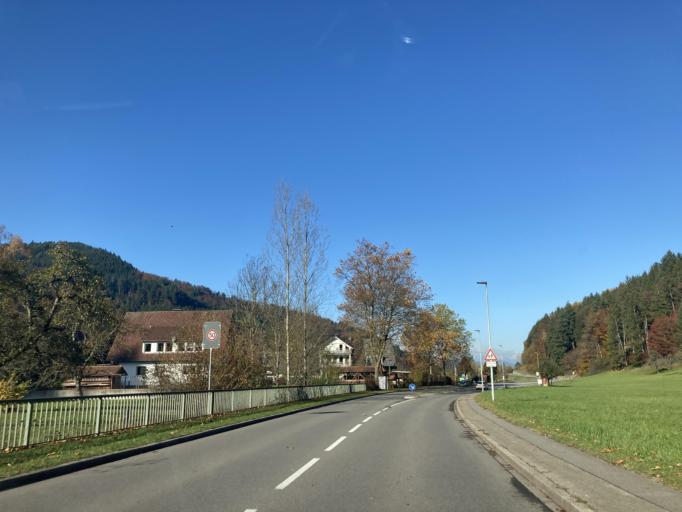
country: DE
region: Baden-Wuerttemberg
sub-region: Freiburg Region
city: Muhlenbach
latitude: 48.2559
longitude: 8.1085
